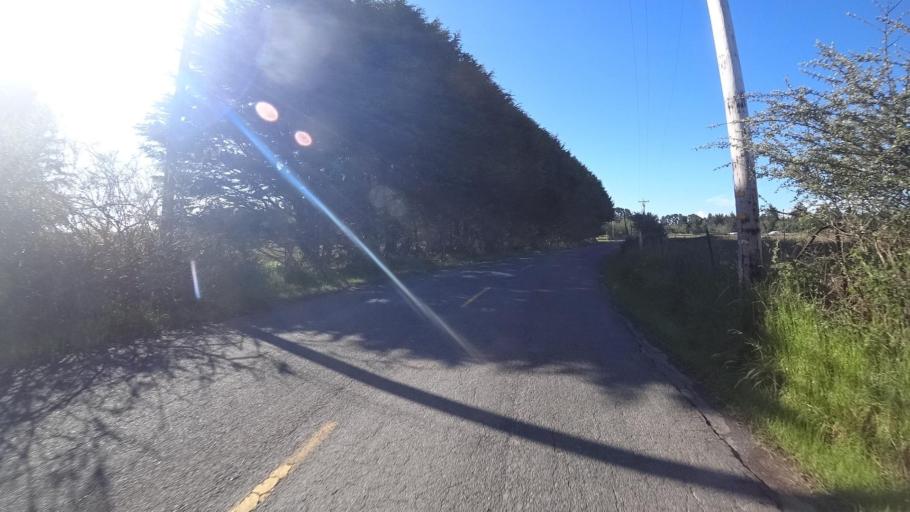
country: US
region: California
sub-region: Humboldt County
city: Westhaven-Moonstone
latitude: 41.0043
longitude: -124.1006
